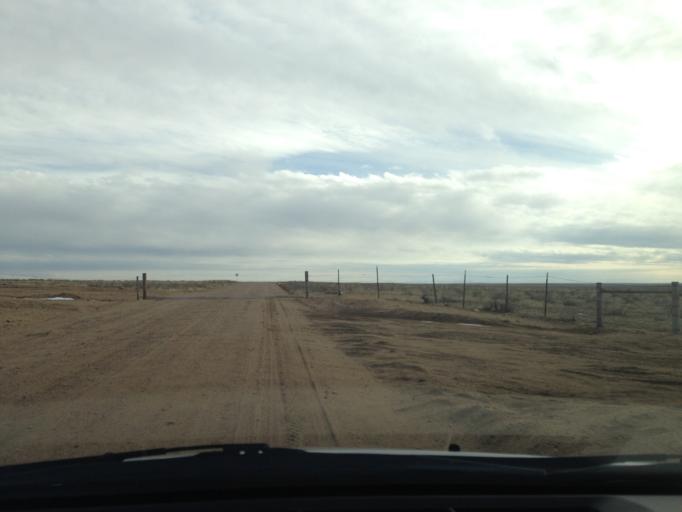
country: US
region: Colorado
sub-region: Weld County
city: Keenesburg
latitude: 40.2470
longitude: -104.2068
